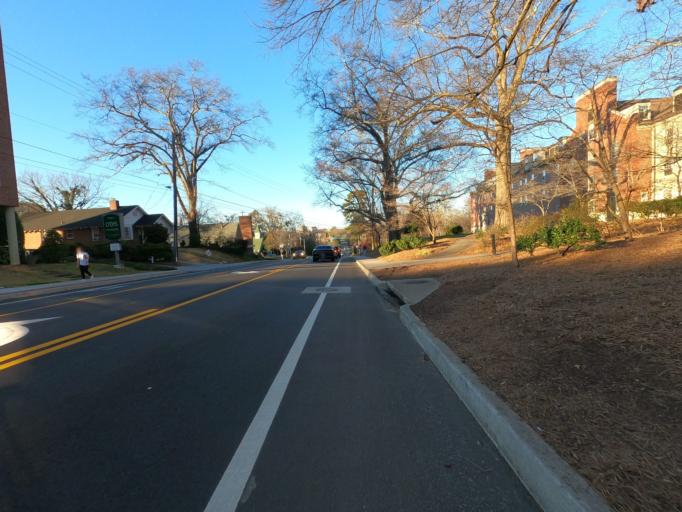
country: US
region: Georgia
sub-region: Clarke County
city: Athens
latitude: 33.9466
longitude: -83.3783
